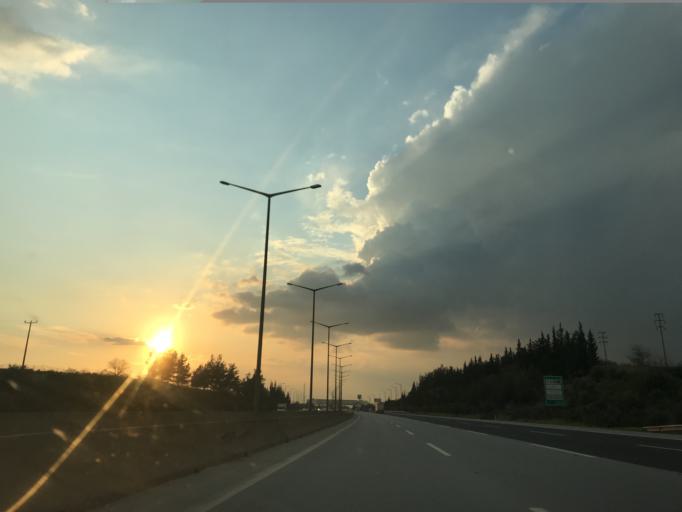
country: TR
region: Adana
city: Seyhan
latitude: 37.0298
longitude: 35.2147
